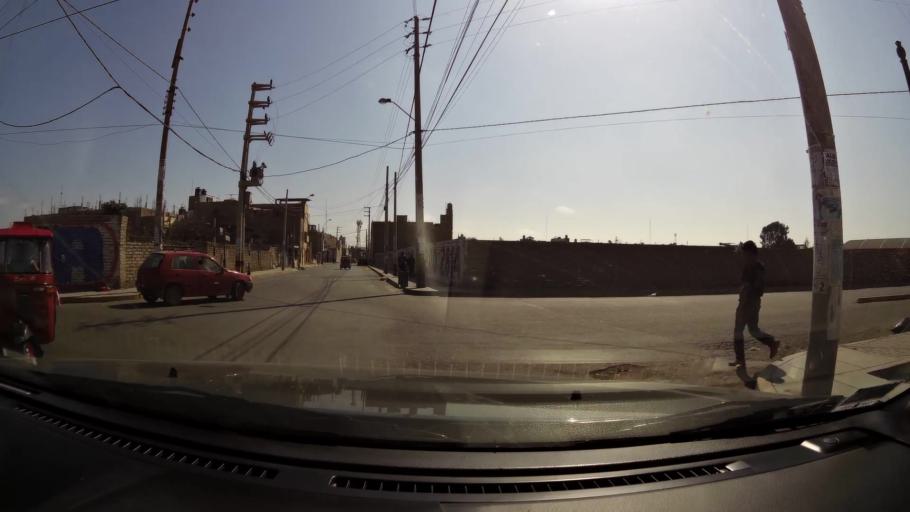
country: PE
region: Ica
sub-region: Provincia de Chincha
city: Chincha Alta
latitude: -13.4155
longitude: -76.1293
